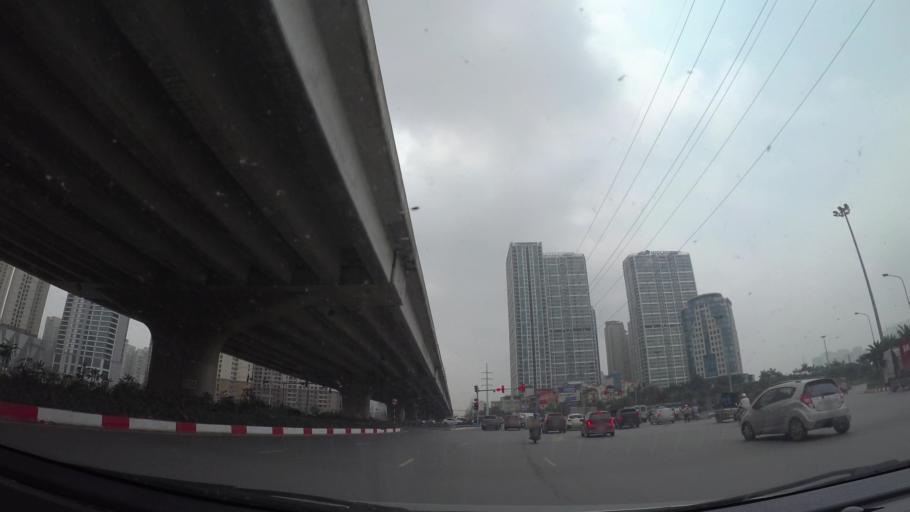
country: VN
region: Ha Noi
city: Thanh Xuan
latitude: 21.0060
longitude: 105.7915
